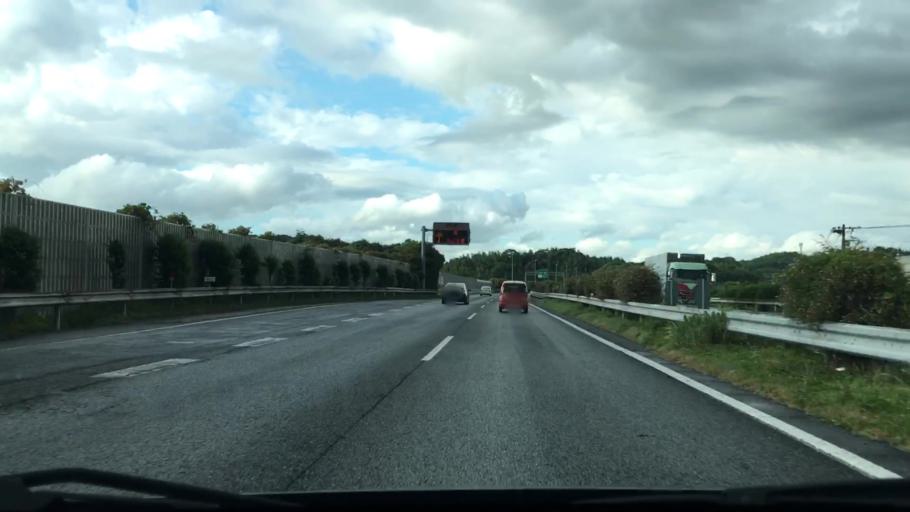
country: JP
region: Fukuoka
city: Koga
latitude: 33.7131
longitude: 130.4899
